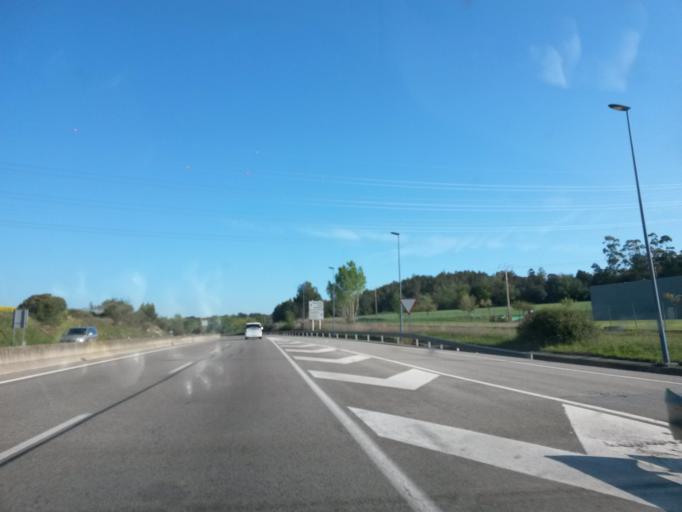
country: ES
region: Catalonia
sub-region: Provincia de Girona
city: Palol de Revardit
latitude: 42.0518
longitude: 2.8183
